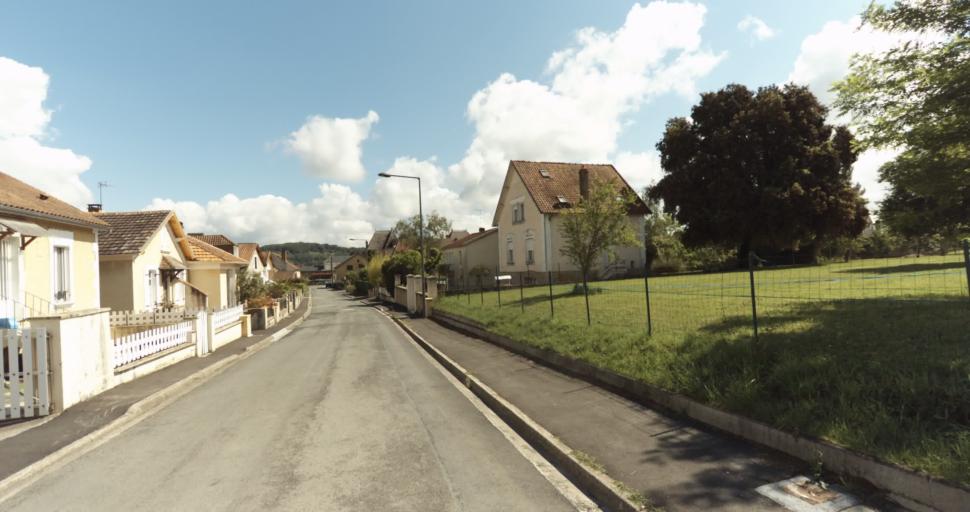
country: FR
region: Aquitaine
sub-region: Departement de la Dordogne
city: Le Bugue
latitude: 44.8448
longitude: 0.9067
